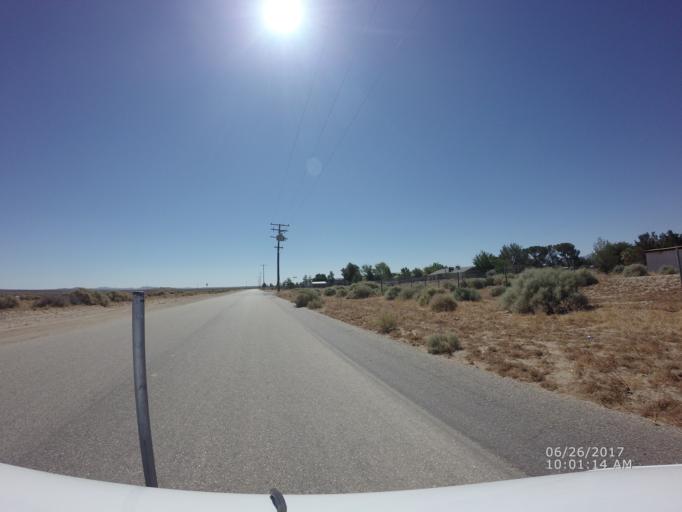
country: US
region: California
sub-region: Los Angeles County
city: Lake Los Angeles
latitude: 34.6312
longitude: -117.8144
